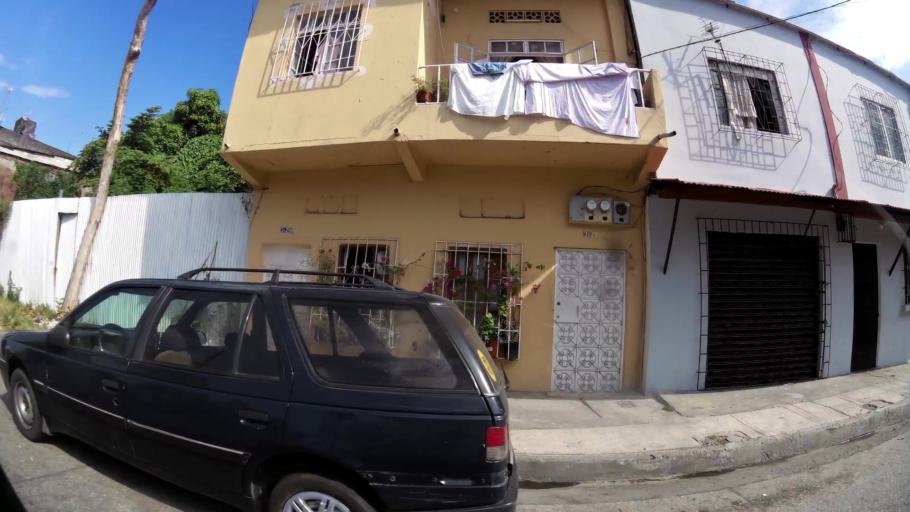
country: EC
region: Guayas
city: Guayaquil
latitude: -2.2126
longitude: -79.9130
